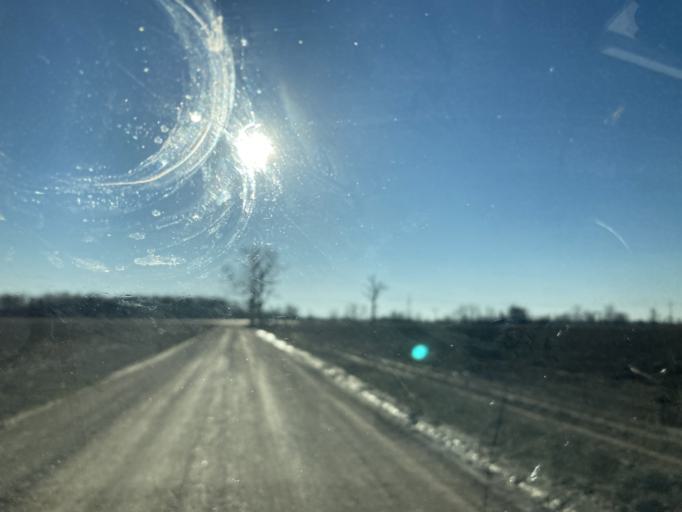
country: US
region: Mississippi
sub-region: Yazoo County
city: Yazoo City
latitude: 32.9237
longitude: -90.6113
